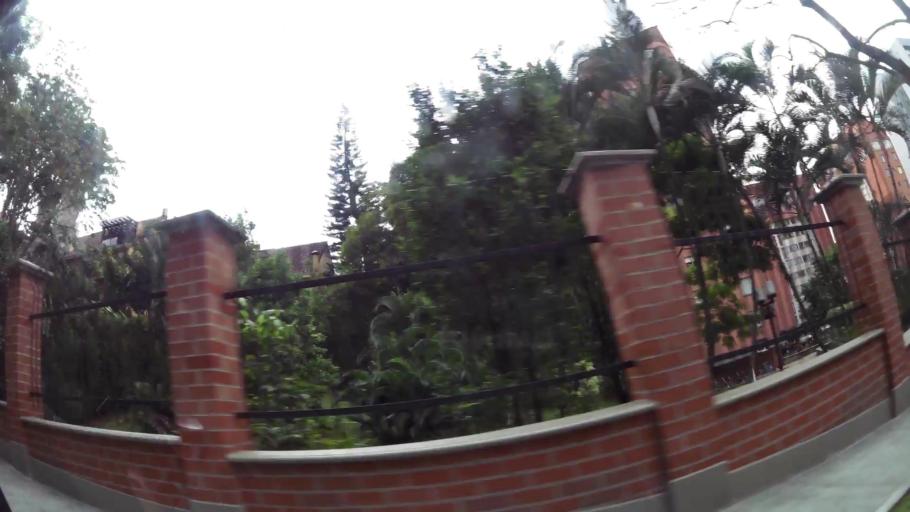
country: CO
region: Antioquia
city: Envigado
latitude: 6.1813
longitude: -75.5741
